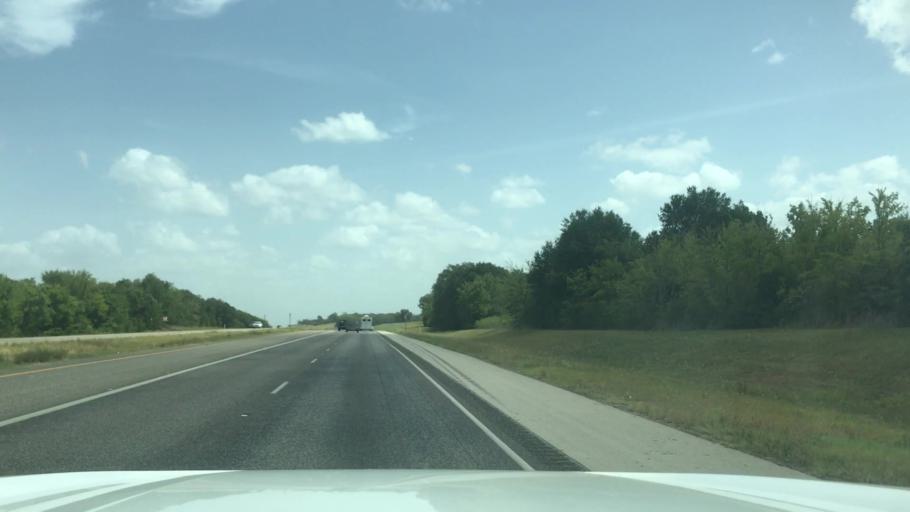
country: US
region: Texas
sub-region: Robertson County
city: Calvert
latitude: 30.9382
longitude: -96.6405
